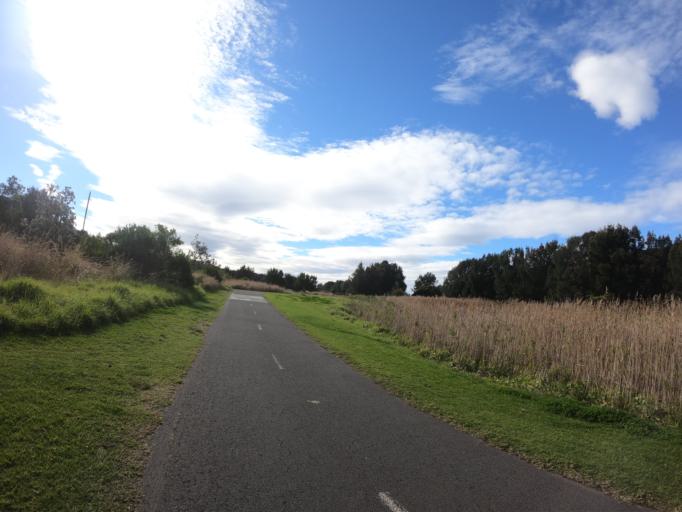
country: AU
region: New South Wales
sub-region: Wollongong
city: Bulli
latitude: -34.3260
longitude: 150.9216
